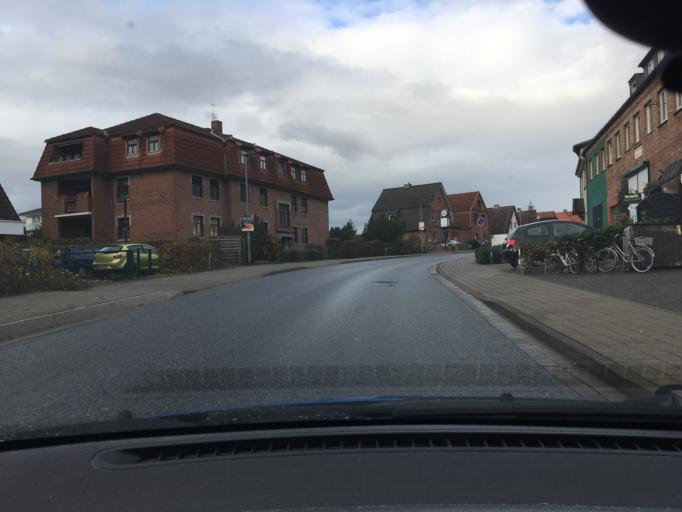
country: DE
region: Schleswig-Holstein
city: Molln
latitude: 53.6335
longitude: 10.6909
